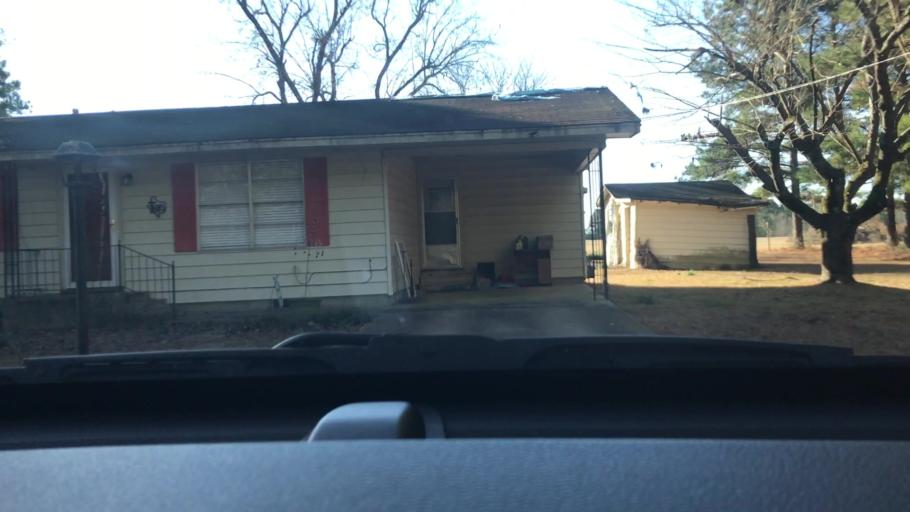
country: US
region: Arkansas
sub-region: Hempstead County
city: Hope
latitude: 33.6386
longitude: -93.5709
